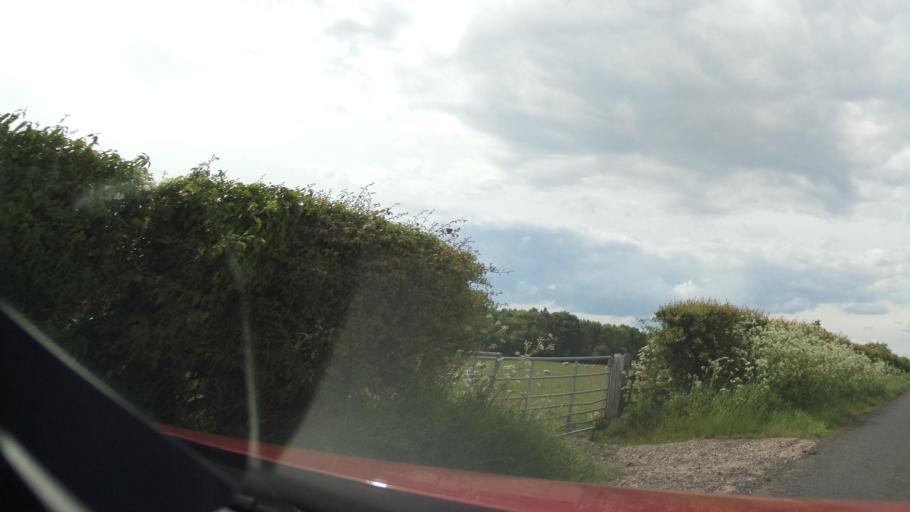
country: GB
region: England
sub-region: Northumberland
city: Alnwick
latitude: 55.4627
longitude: -1.7164
